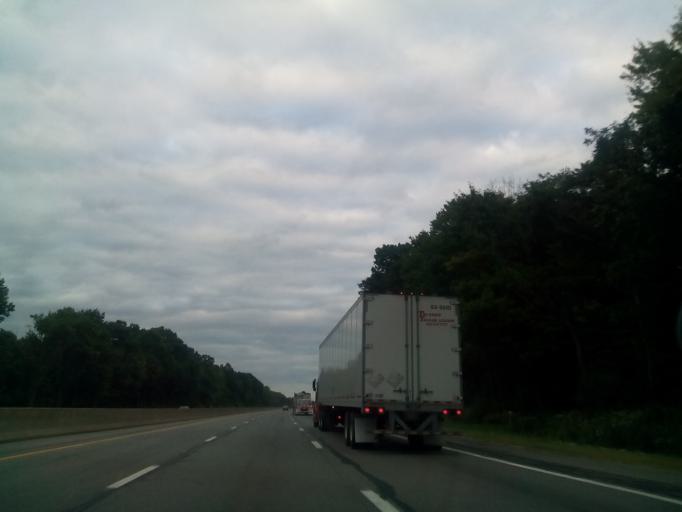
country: US
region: Ohio
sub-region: Portage County
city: Garrettsville
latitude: 41.2440
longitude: -81.0950
